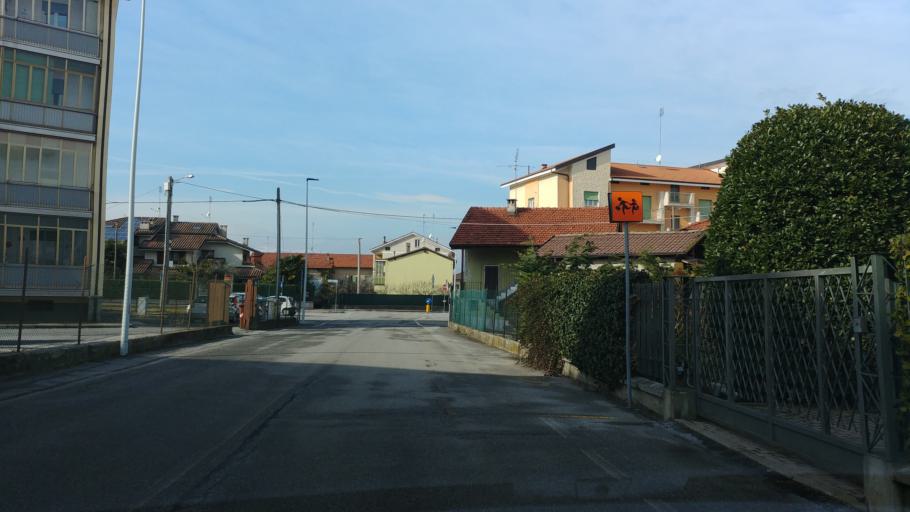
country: IT
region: Piedmont
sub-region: Provincia di Cuneo
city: Cuneo
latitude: 44.3976
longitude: 7.5743
